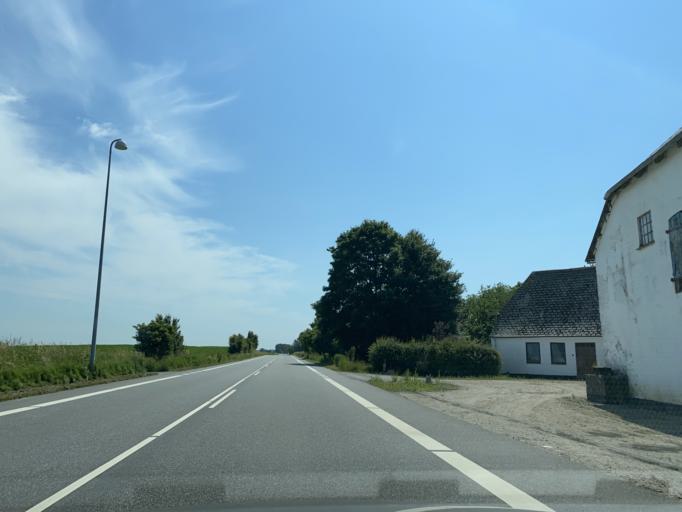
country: DK
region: South Denmark
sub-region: Sonderborg Kommune
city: Grasten
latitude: 54.9938
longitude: 9.5896
